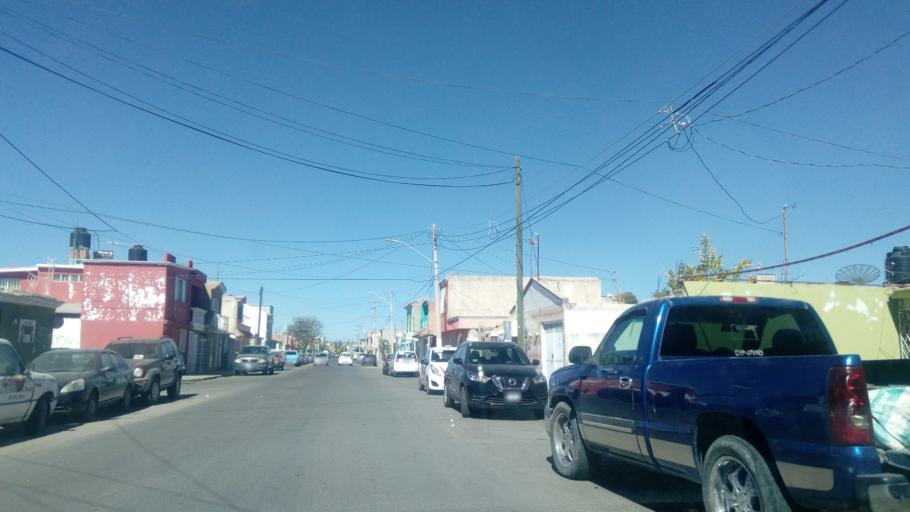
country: MX
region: Durango
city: Victoria de Durango
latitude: 24.0173
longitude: -104.6409
